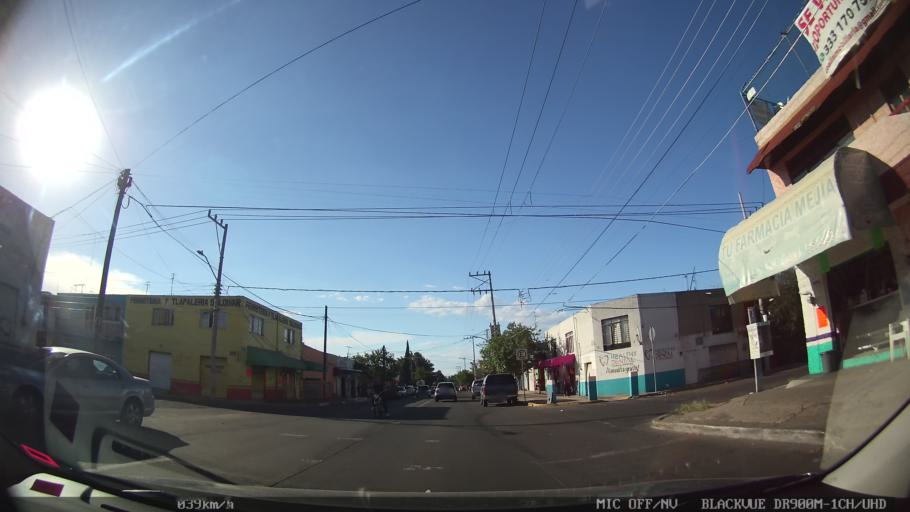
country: MX
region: Jalisco
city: Tlaquepaque
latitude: 20.7087
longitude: -103.2962
